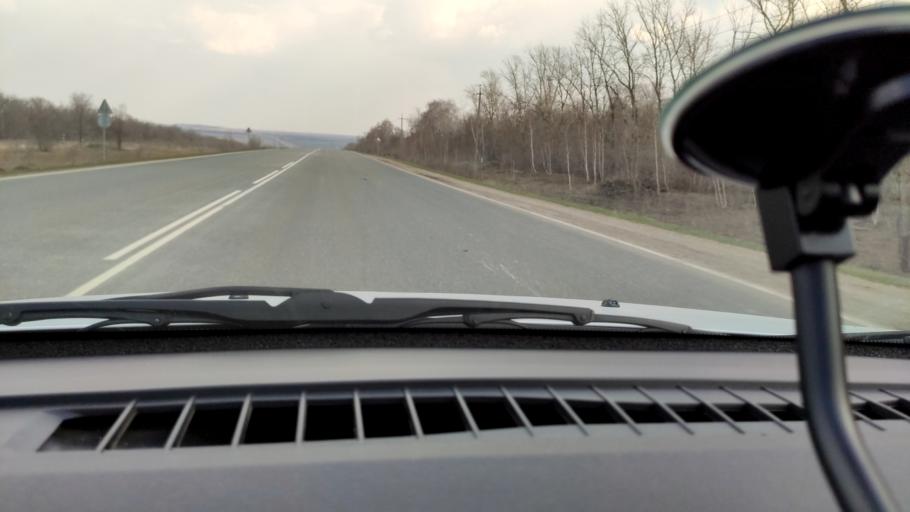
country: RU
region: Samara
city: Dubovyy Umet
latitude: 53.0789
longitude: 50.3505
